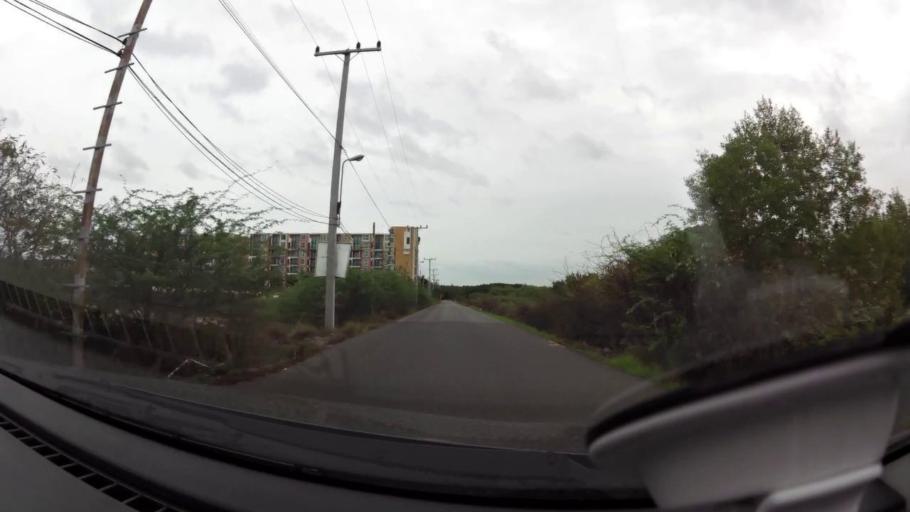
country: TH
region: Prachuap Khiri Khan
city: Pran Buri
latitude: 12.4212
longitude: 99.9799
